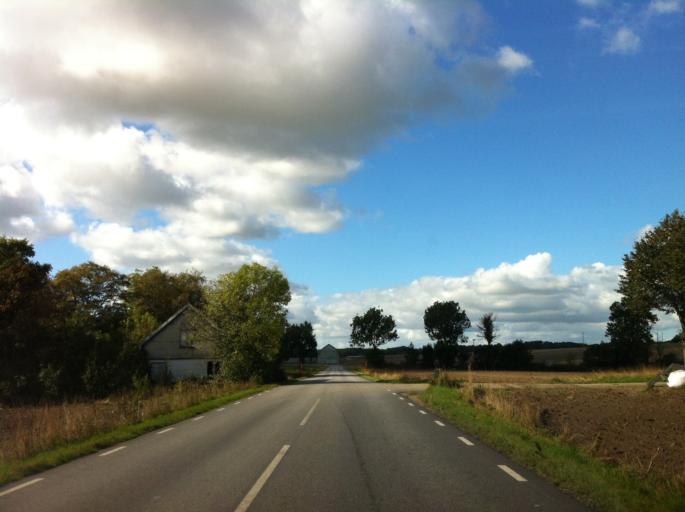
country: SE
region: Skane
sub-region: Tomelilla Kommun
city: Tomelilla
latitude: 55.6477
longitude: 13.9675
